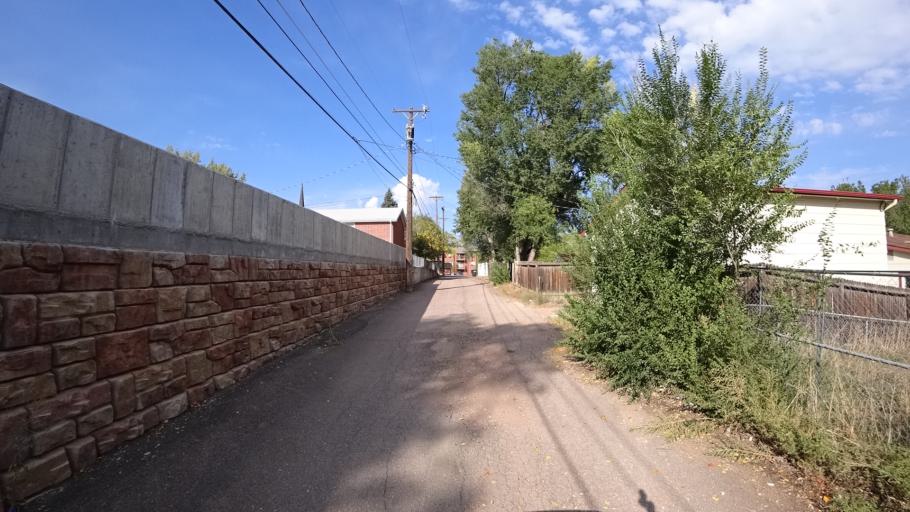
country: US
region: Colorado
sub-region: El Paso County
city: Colorado Springs
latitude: 38.8547
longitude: -104.7840
